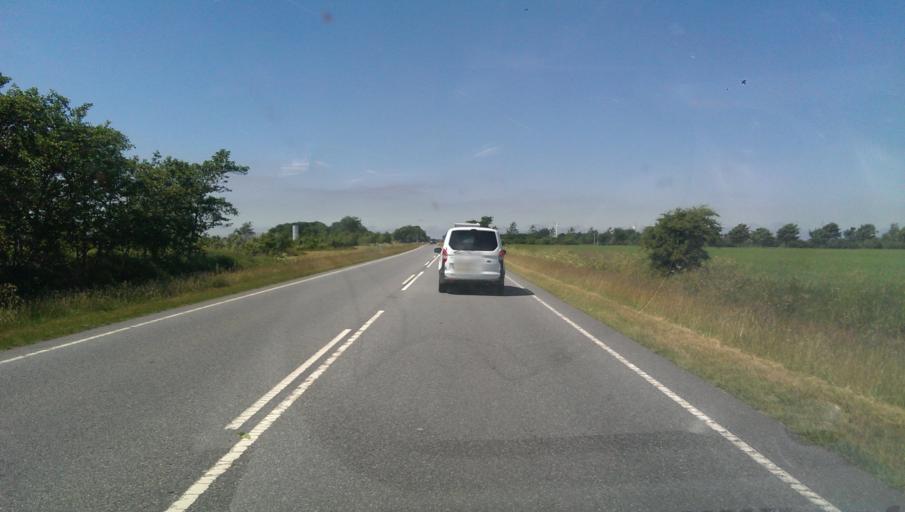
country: DK
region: South Denmark
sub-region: Esbjerg Kommune
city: Esbjerg
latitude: 55.5348
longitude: 8.4195
